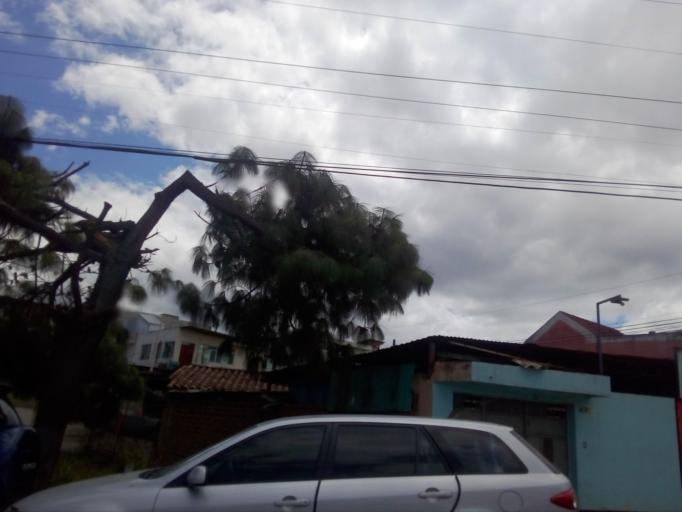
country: GT
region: Quetzaltenango
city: Quetzaltenango
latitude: 14.8577
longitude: -91.5107
